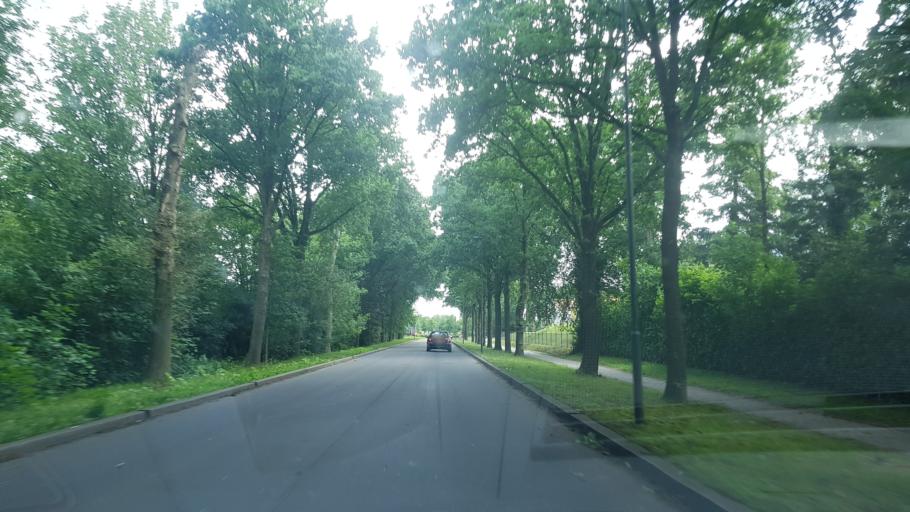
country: NL
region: Friesland
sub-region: Gemeente Tytsjerksteradiel
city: Gytsjerk
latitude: 53.2434
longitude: 5.8970
